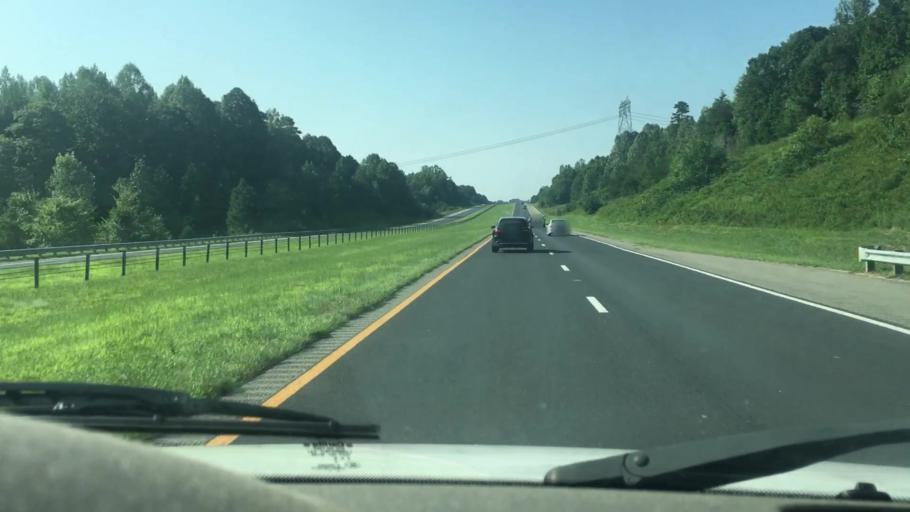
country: US
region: North Carolina
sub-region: Lincoln County
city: Lowesville
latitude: 35.4128
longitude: -80.9986
